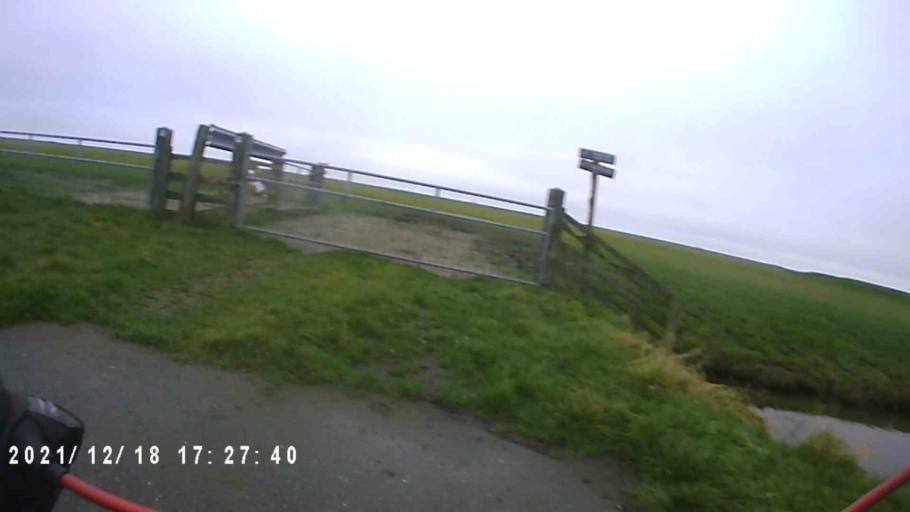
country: NL
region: Friesland
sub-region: Gemeente Ferwerderadiel
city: Ferwert
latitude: 53.3646
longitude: 5.8548
